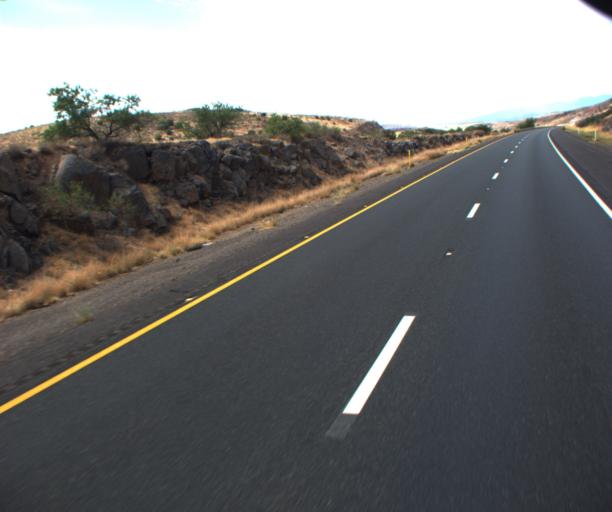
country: US
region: Arizona
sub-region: Yavapai County
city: Cordes Lakes
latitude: 34.4652
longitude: -112.0281
